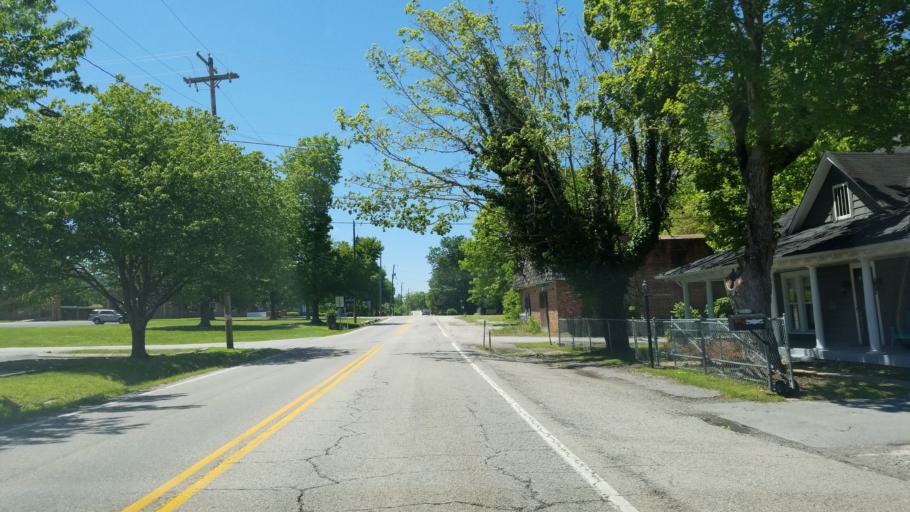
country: US
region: Tennessee
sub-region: Hamilton County
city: Collegedale
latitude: 35.0739
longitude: -85.0624
